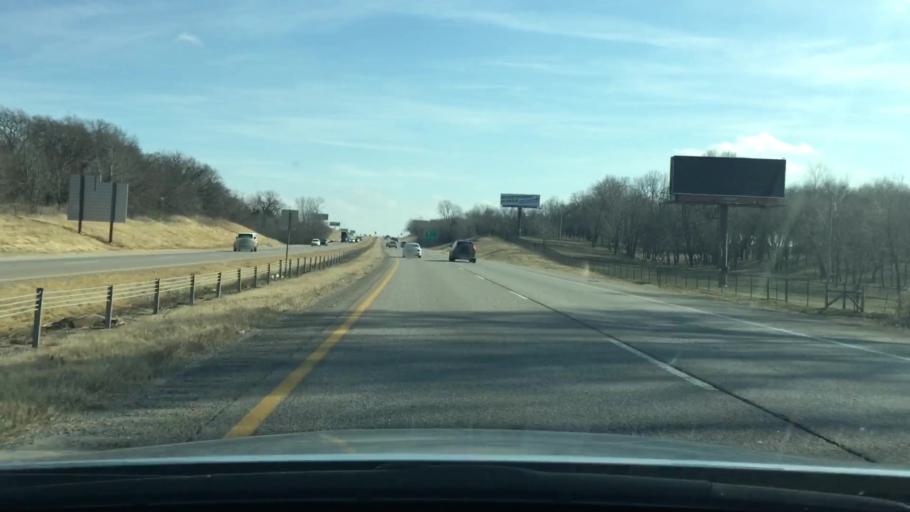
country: US
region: Oklahoma
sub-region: McClain County
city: Goldsby
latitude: 35.1685
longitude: -97.4911
